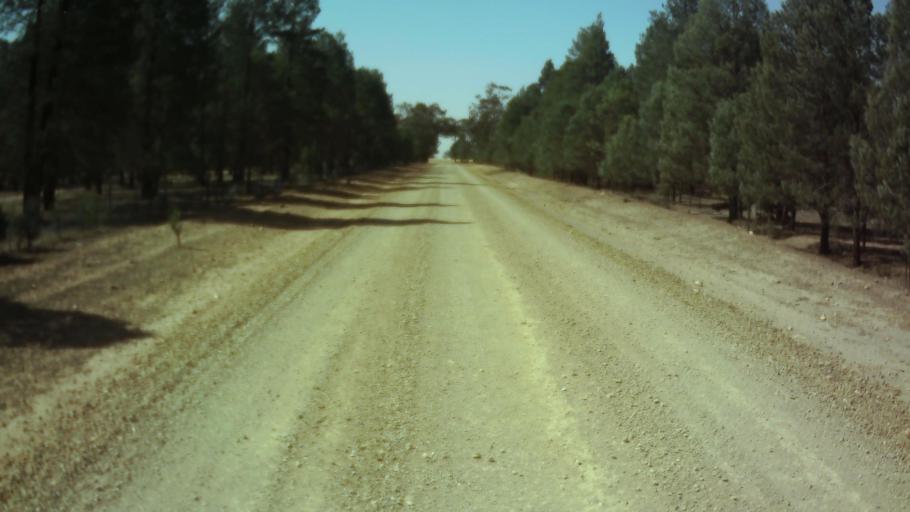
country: AU
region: New South Wales
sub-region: Weddin
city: Grenfell
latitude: -33.9616
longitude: 147.9320
